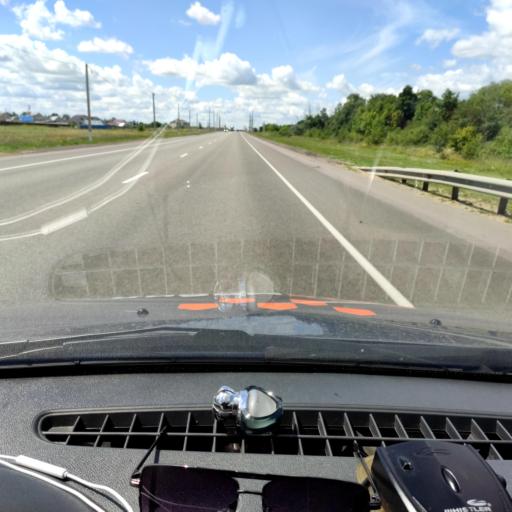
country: RU
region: Lipetsk
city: Borinskoye
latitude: 52.4649
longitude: 39.3356
